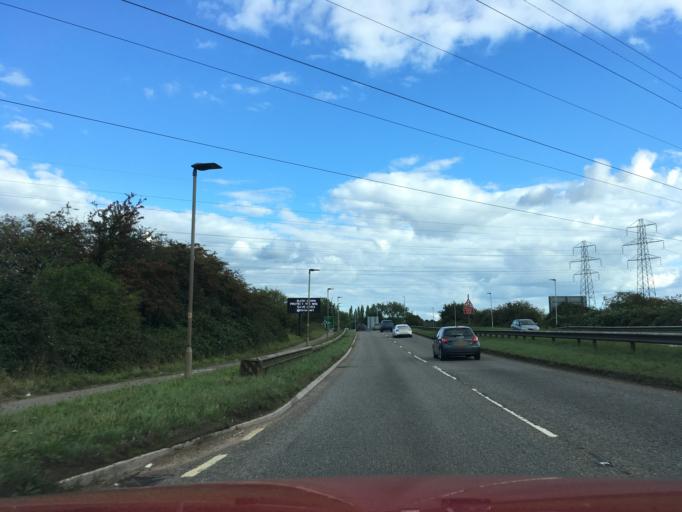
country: GB
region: England
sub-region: Devon
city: Topsham
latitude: 50.7113
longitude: -3.4607
